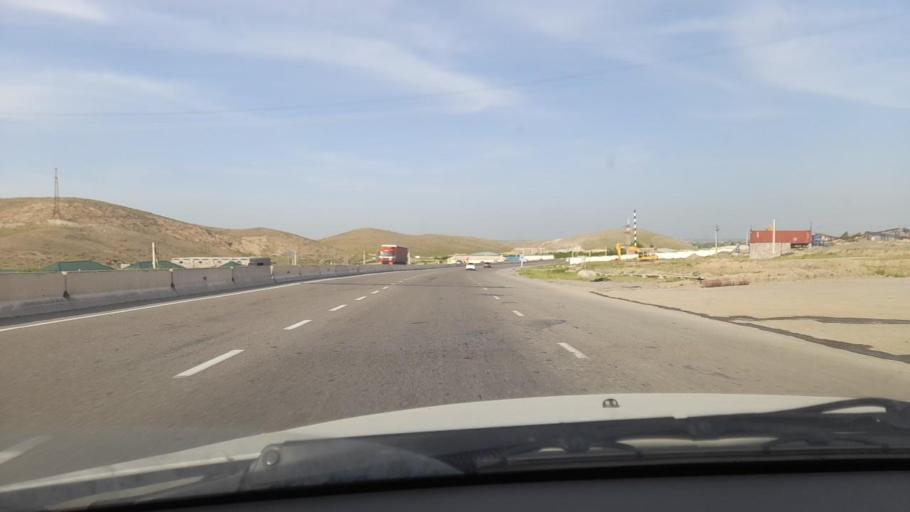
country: UZ
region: Jizzax
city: Jizzax
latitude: 40.0648
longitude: 67.8426
